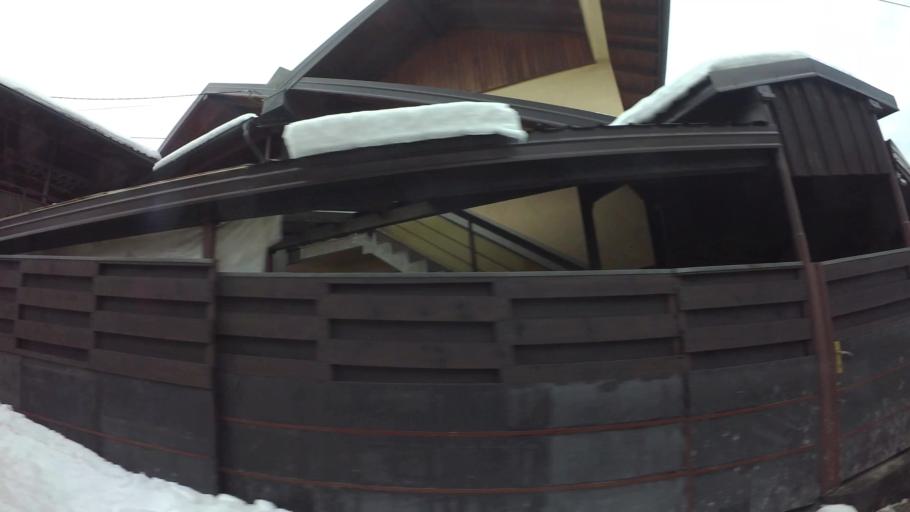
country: BA
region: Federation of Bosnia and Herzegovina
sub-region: Kanton Sarajevo
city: Sarajevo
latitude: 43.8676
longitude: 18.3203
